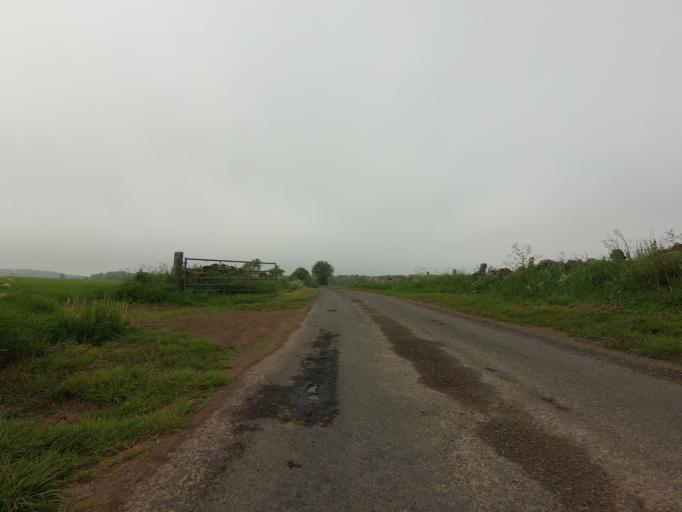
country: GB
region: Scotland
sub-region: Fife
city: Ballingry
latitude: 56.2491
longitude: -3.3353
